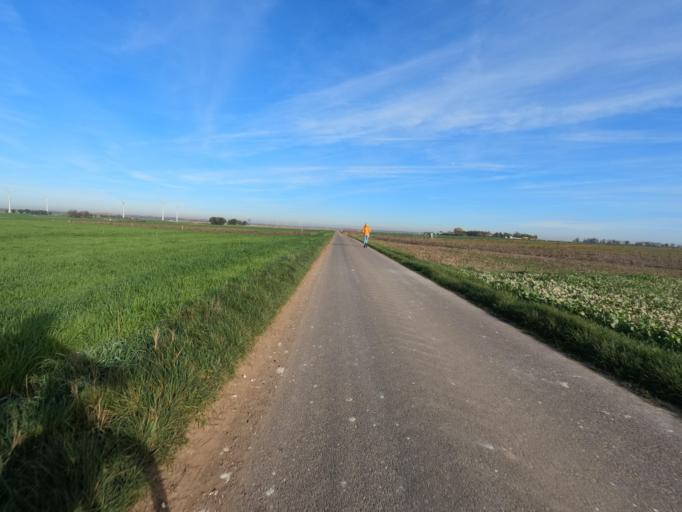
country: DE
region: North Rhine-Westphalia
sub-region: Regierungsbezirk Koln
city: Titz
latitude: 51.0519
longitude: 6.4147
